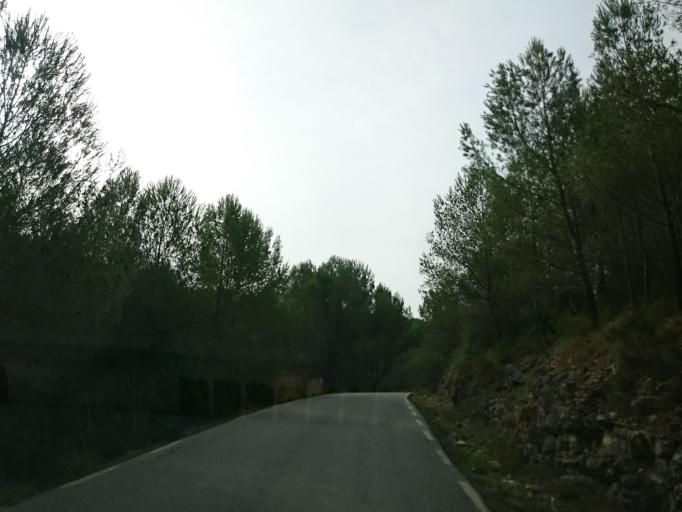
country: ES
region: Catalonia
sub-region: Provincia de Barcelona
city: Olivella
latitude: 41.3103
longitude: 1.8173
